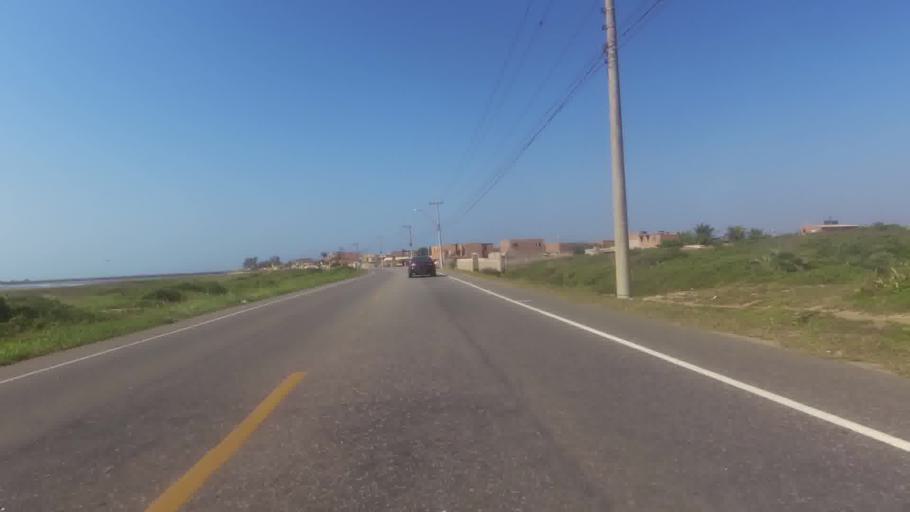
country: BR
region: Espirito Santo
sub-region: Itapemirim
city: Itapemirim
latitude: -20.9970
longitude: -40.8098
